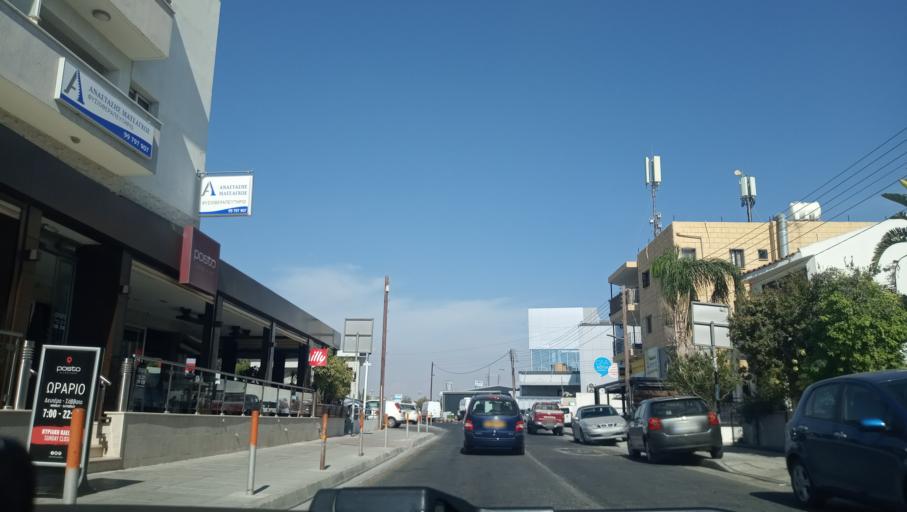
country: CY
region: Larnaka
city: Livadia
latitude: 34.9476
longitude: 33.6280
